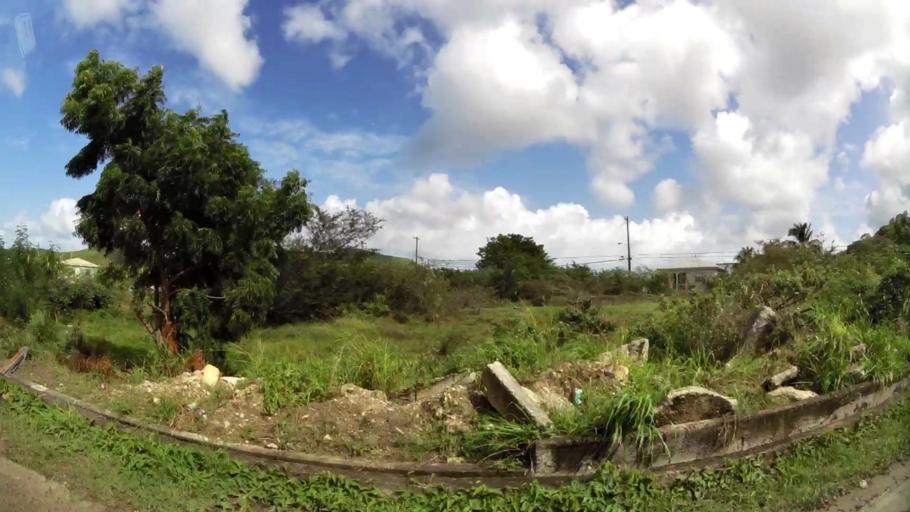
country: AG
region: Saint Mary
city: Bolands
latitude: 17.0698
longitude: -61.8745
